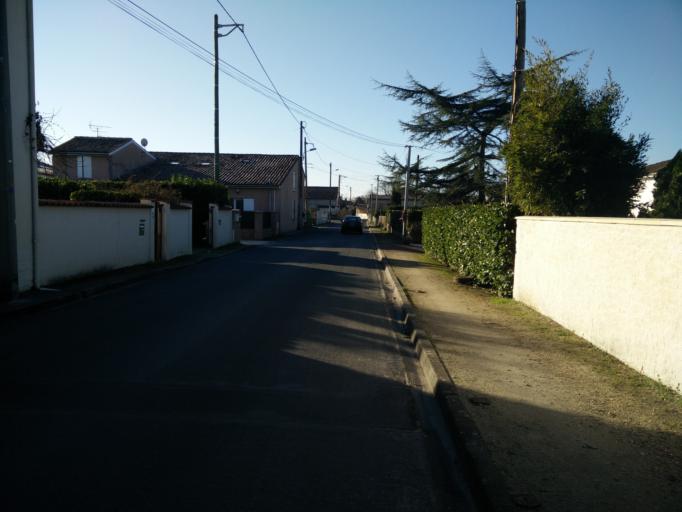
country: FR
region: Aquitaine
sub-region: Departement de la Gironde
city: Libourne
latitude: 44.9544
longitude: -0.2356
